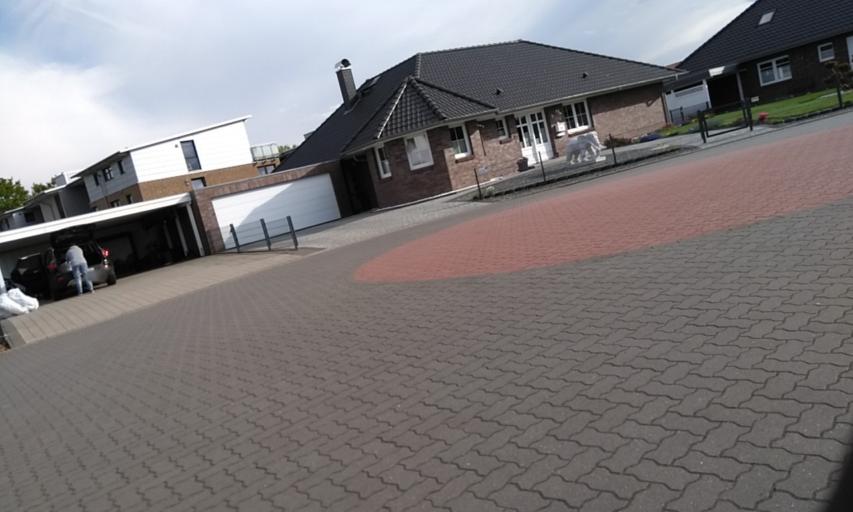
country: DE
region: Lower Saxony
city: Apensen
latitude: 53.4431
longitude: 9.6286
